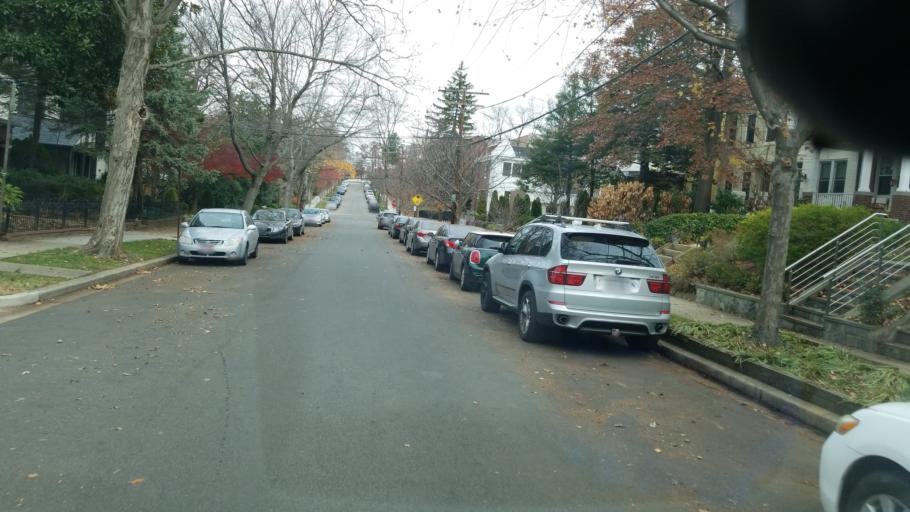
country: US
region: Maryland
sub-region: Montgomery County
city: Friendship Village
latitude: 38.9262
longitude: -77.0767
